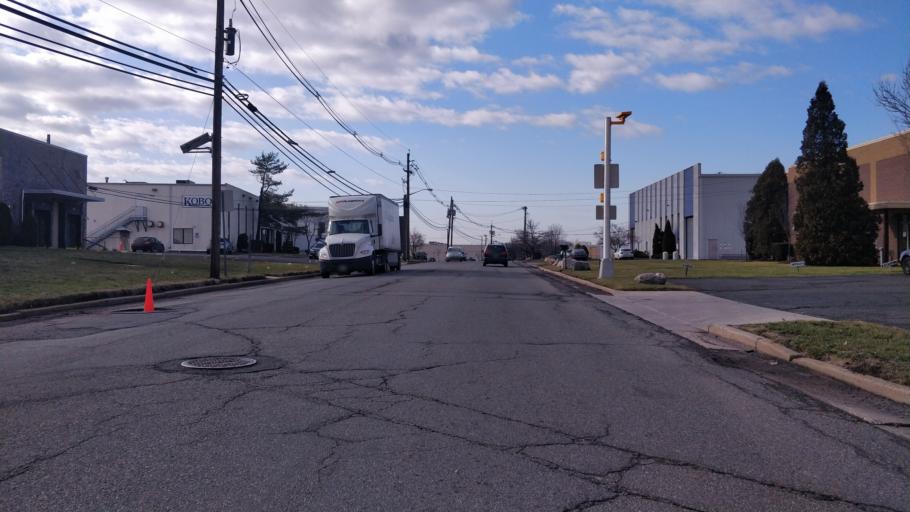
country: US
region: New Jersey
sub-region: Middlesex County
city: South Plainfield
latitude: 40.5627
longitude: -74.4188
